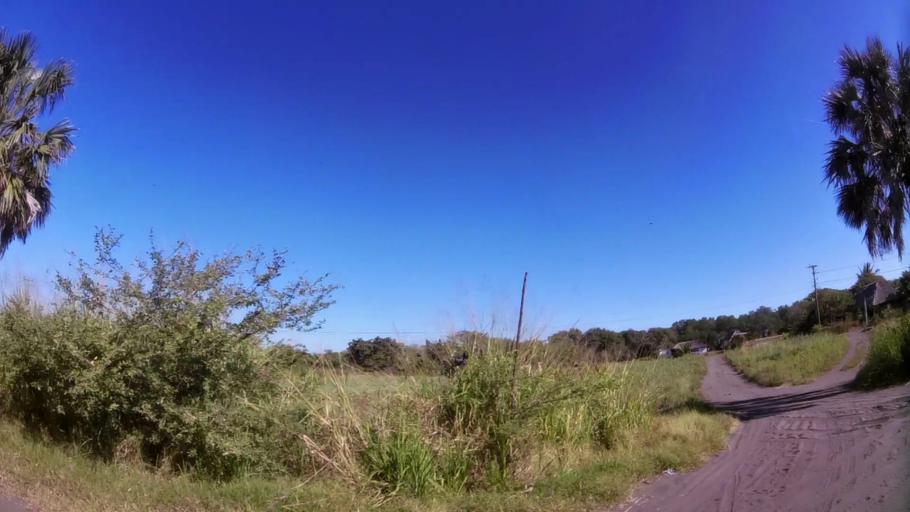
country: GT
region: Santa Rosa
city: Guazacapan
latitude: 13.8602
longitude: -90.3964
